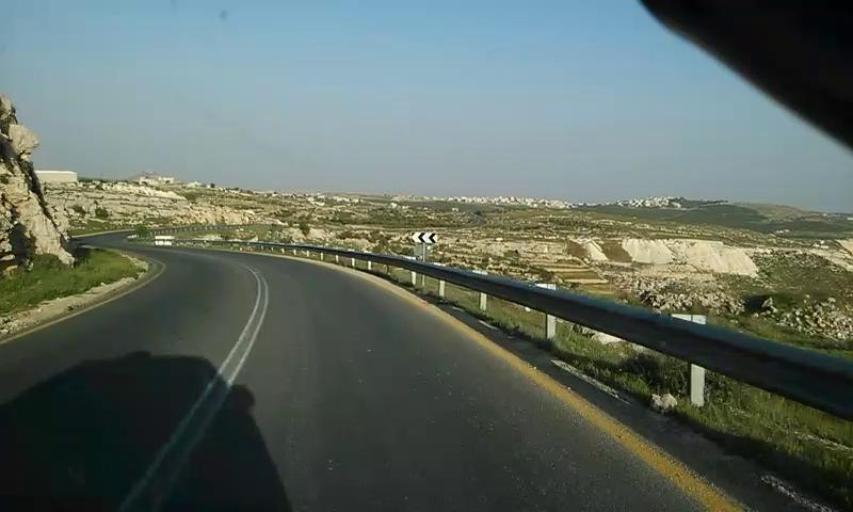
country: PS
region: West Bank
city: Jurat ash Sham`ah
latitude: 31.6472
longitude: 35.1816
